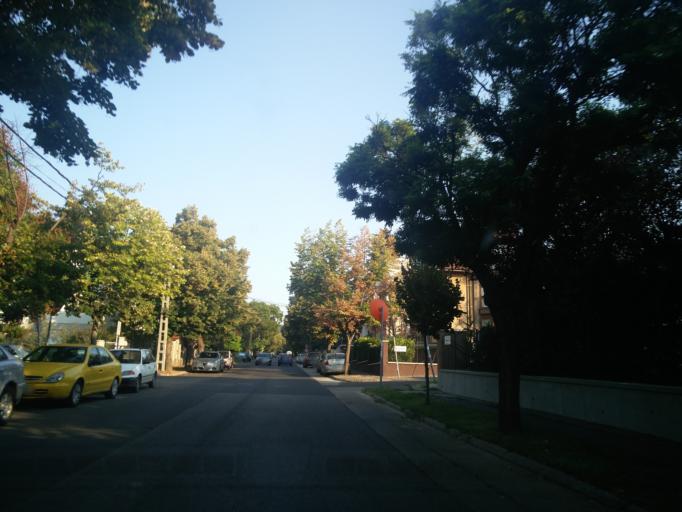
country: HU
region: Budapest
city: Budapest XII. keruelet
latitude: 47.4719
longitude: 19.0100
